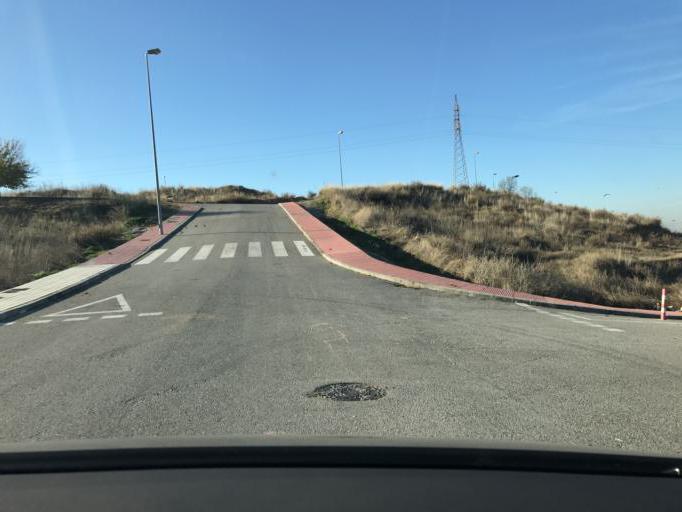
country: ES
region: Andalusia
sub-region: Provincia de Granada
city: Peligros
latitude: 37.2374
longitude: -3.6170
